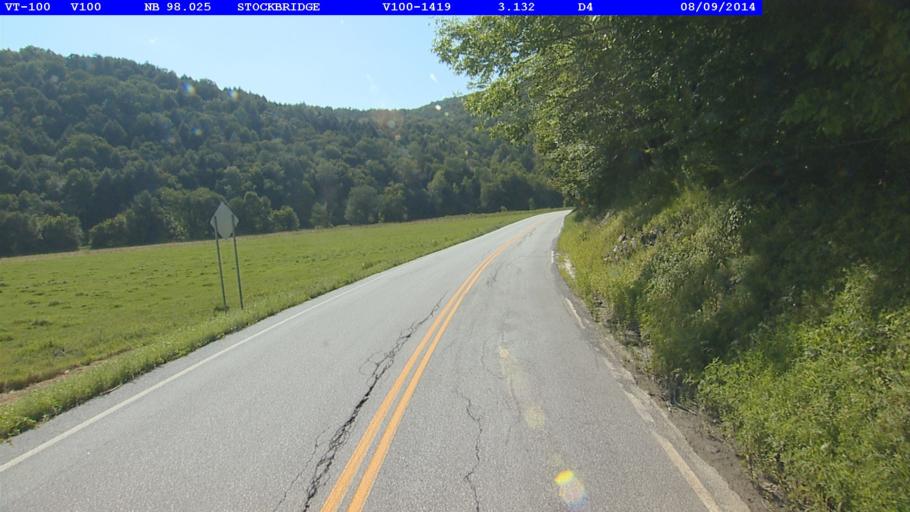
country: US
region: Vermont
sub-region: Orange County
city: Randolph
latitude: 43.7855
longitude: -72.7570
